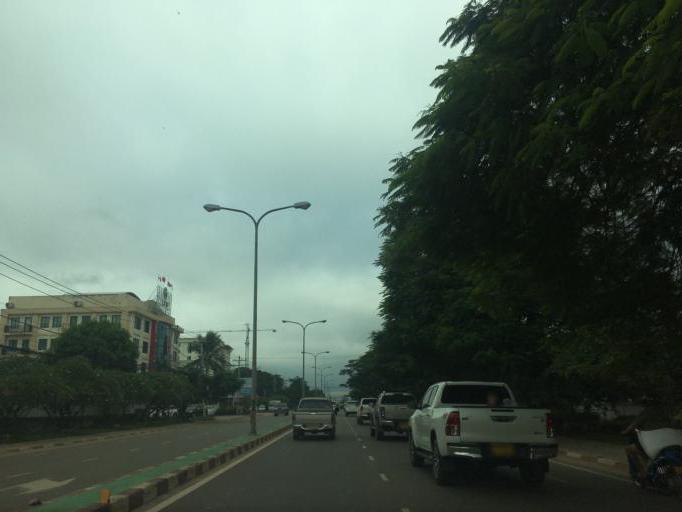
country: TH
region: Nong Khai
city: Si Chiang Mai
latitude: 17.9707
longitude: 102.5705
